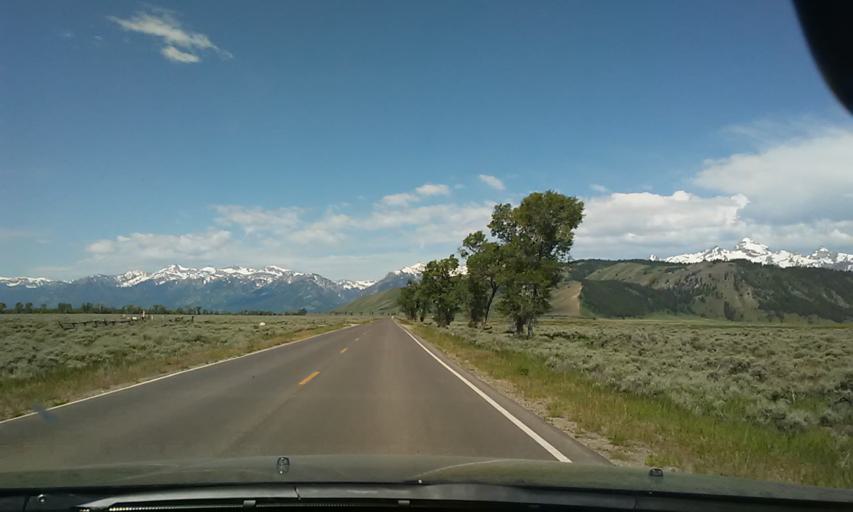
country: US
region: Wyoming
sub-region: Teton County
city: Jackson
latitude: 43.6251
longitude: -110.6374
